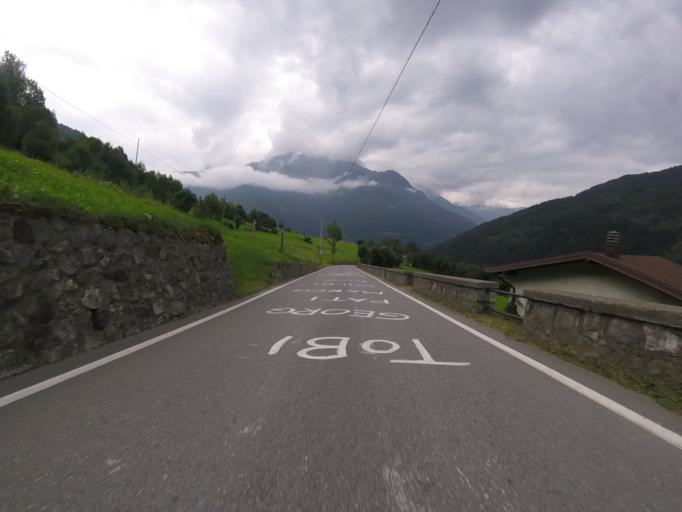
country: IT
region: Lombardy
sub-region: Provincia di Brescia
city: Monno
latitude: 46.2155
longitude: 10.3296
